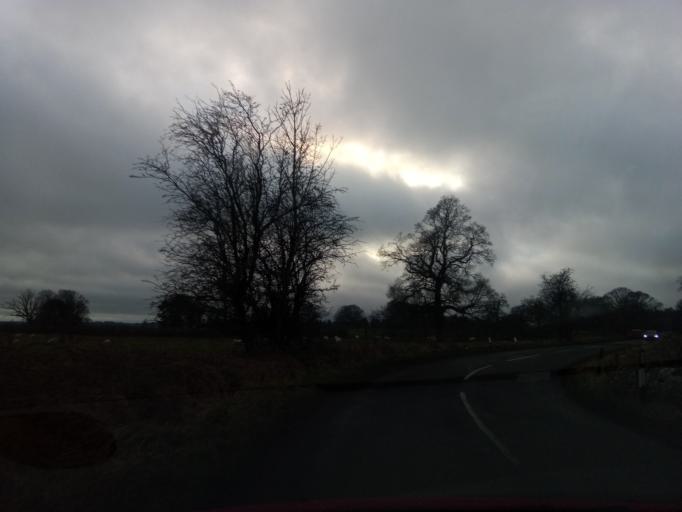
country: GB
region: England
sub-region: Northumberland
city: Hartburn
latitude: 55.1360
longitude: -1.8558
